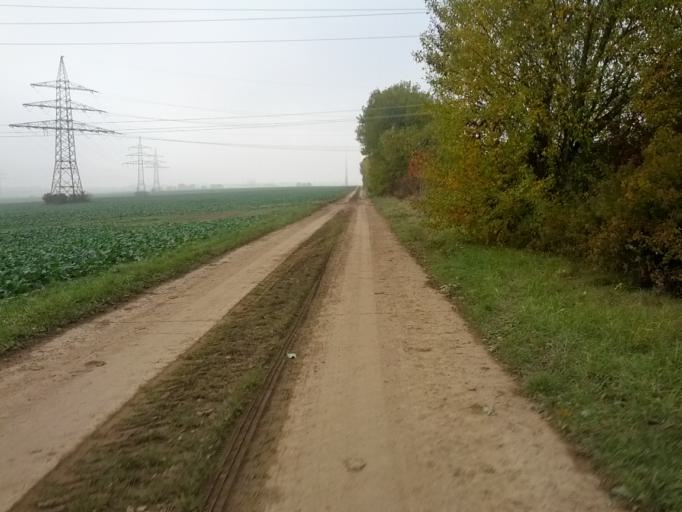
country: DE
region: Thuringia
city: Bischofroda
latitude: 51.0008
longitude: 10.3864
